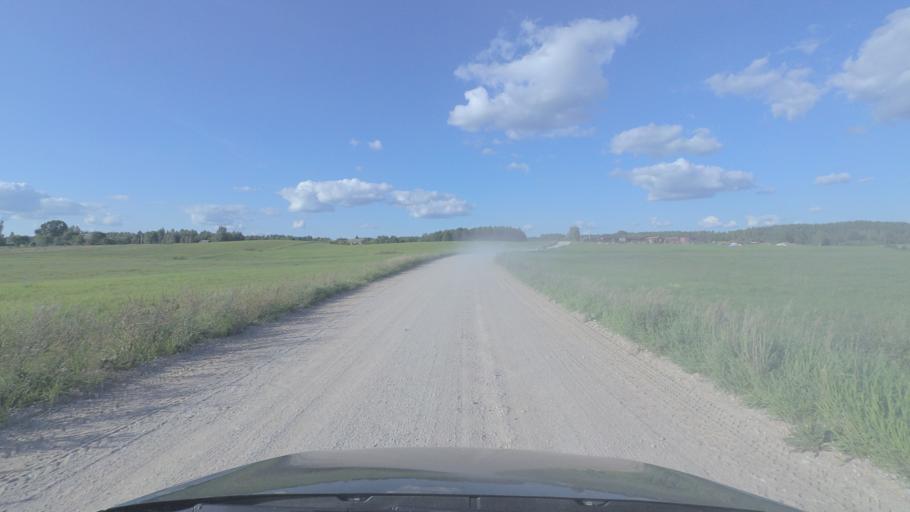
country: LT
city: Pabrade
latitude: 55.1346
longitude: 25.7077
